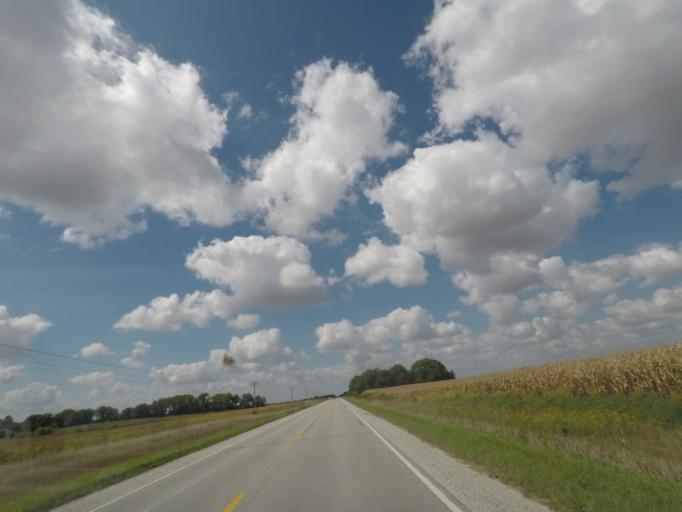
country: US
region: Iowa
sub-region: Story County
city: Nevada
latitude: 42.0226
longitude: -93.3485
